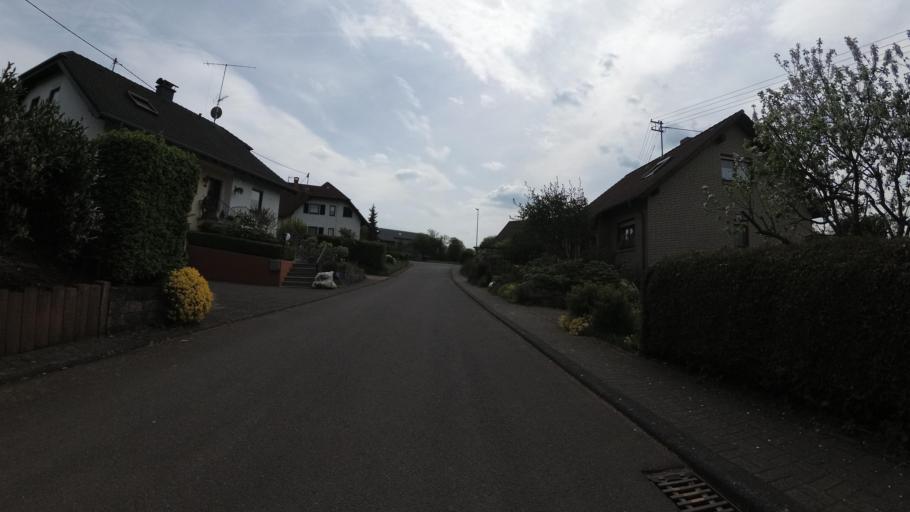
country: DE
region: Rheinland-Pfalz
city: Fohren-Linden
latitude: 49.5845
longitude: 7.2903
